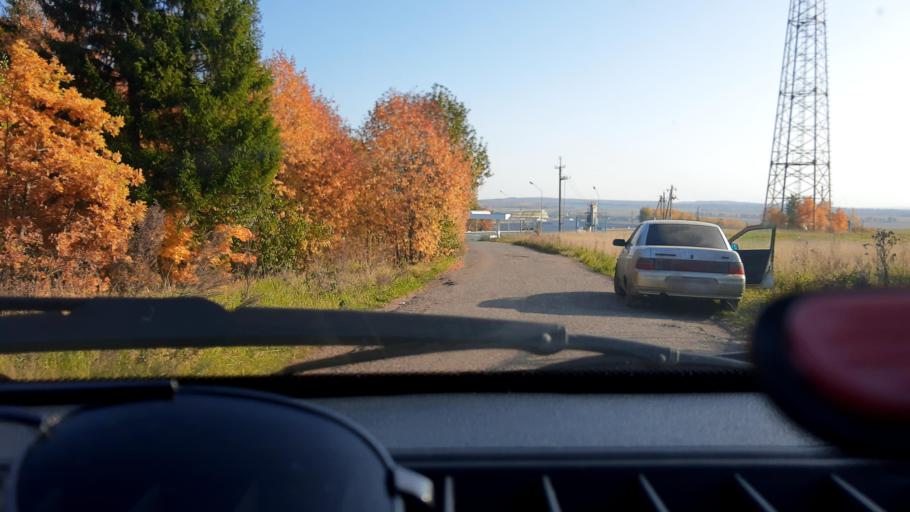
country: RU
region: Bashkortostan
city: Karmaskaly
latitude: 54.3768
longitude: 55.9149
